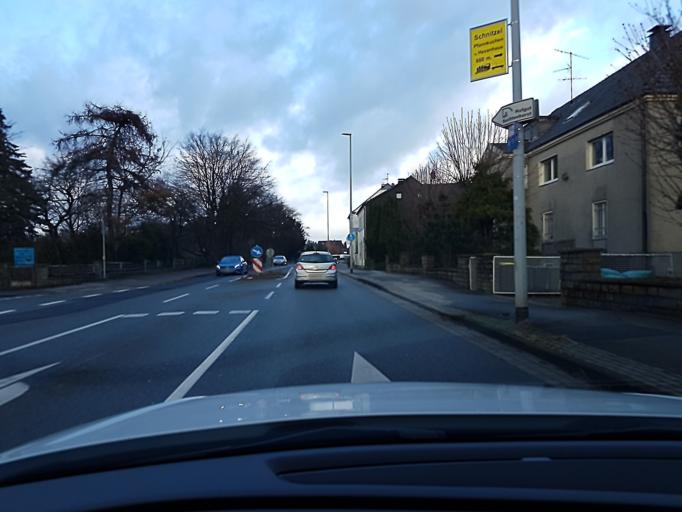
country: DE
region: North Rhine-Westphalia
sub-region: Regierungsbezirk Dusseldorf
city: Muelheim (Ruhr)
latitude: 51.3783
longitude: 6.8626
